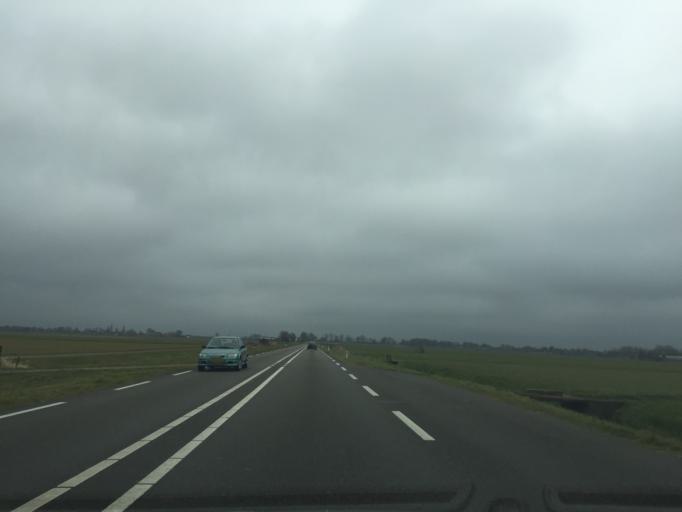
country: NL
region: South Holland
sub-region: Gemeente Kaag en Braassem
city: Leimuiden
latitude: 52.2051
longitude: 4.6786
